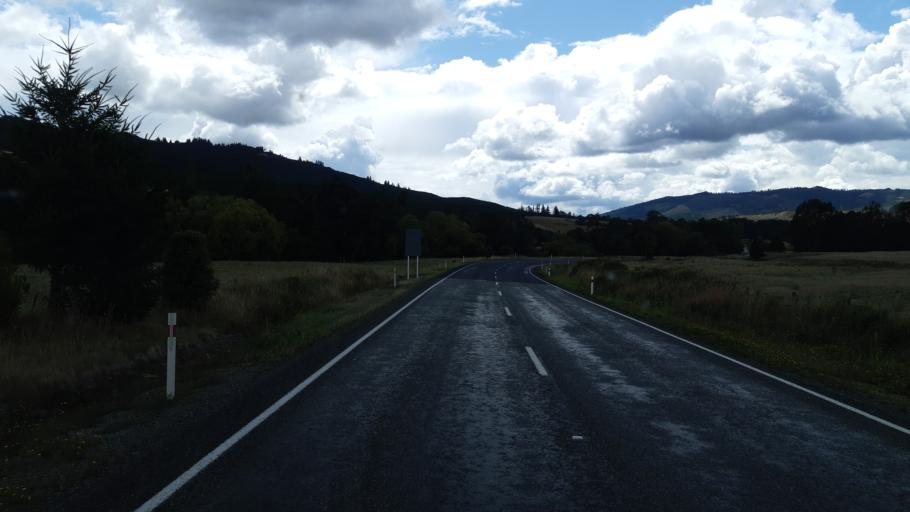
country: NZ
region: Tasman
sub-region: Tasman District
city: Wakefield
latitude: -41.5640
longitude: 172.7786
